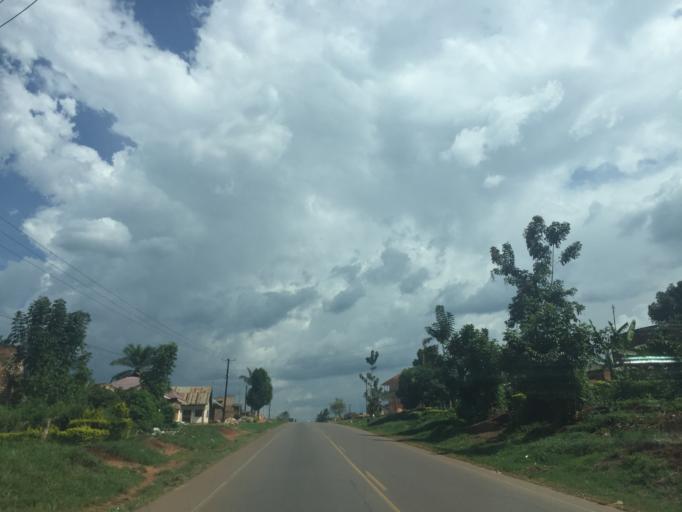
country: UG
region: Central Region
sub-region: Luwero District
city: Wobulenzi
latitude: 0.7354
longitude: 32.5228
